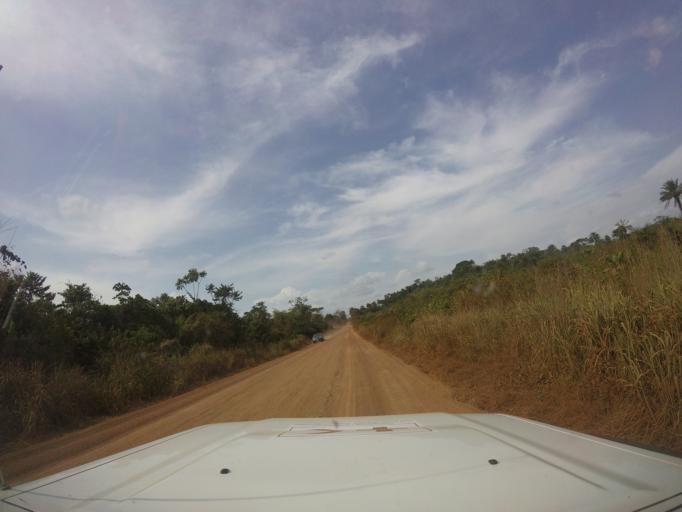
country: LR
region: Grand Cape Mount
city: Robertsport
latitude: 6.7074
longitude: -11.0877
